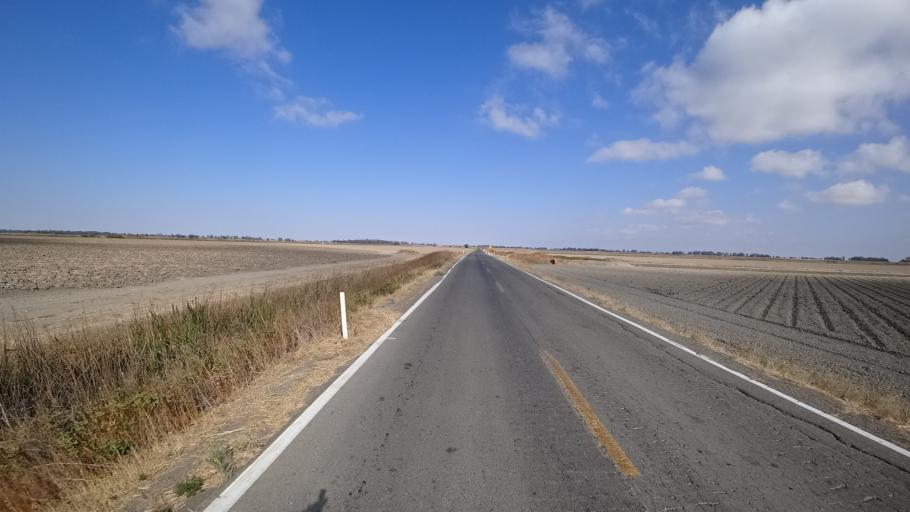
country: US
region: California
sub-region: Yolo County
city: Woodland
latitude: 38.8360
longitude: -121.7520
